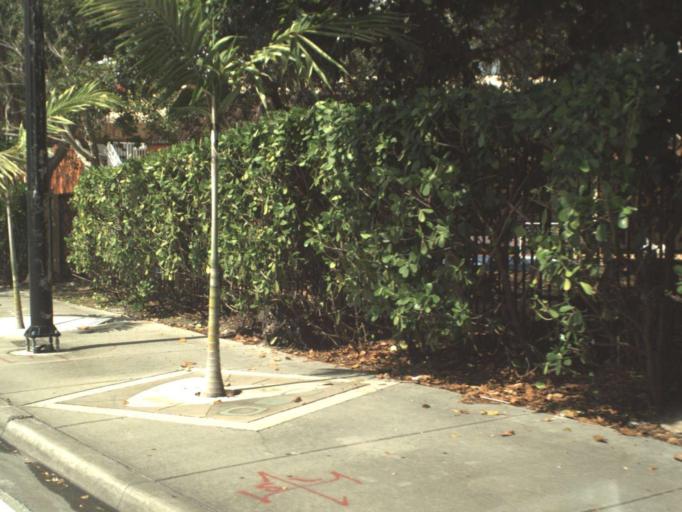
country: US
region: Florida
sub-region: Miami-Dade County
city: El Portal
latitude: 25.8316
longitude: -80.1842
